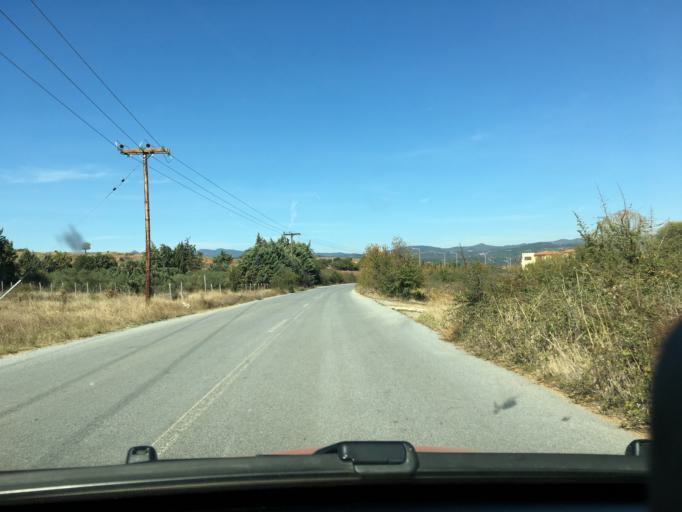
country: GR
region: Central Macedonia
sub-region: Nomos Chalkidikis
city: Megali Panagia
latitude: 40.3583
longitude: 23.7031
